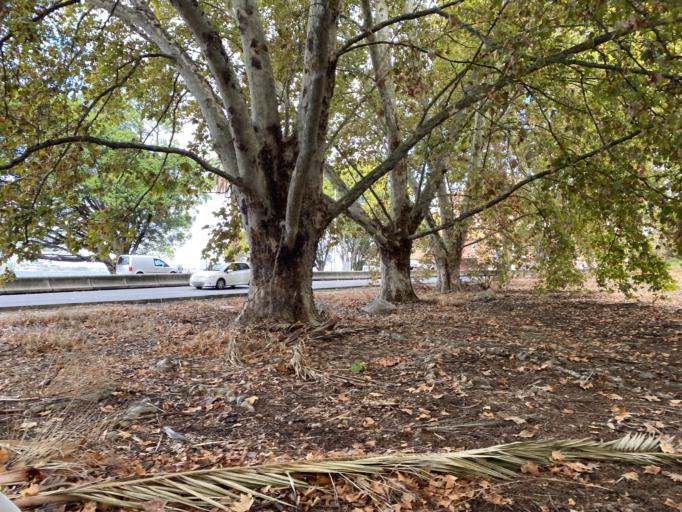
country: AU
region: Western Australia
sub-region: City of Perth
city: West Perth
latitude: -31.9636
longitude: 115.8416
